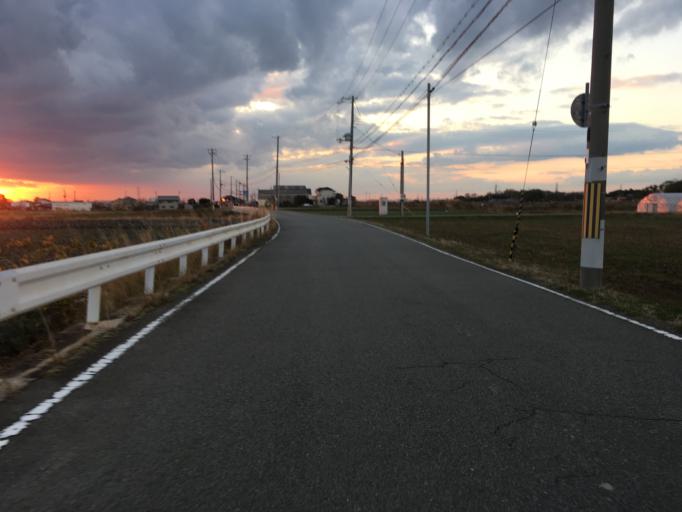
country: JP
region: Hyogo
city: Miki
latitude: 34.7377
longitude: 134.9490
